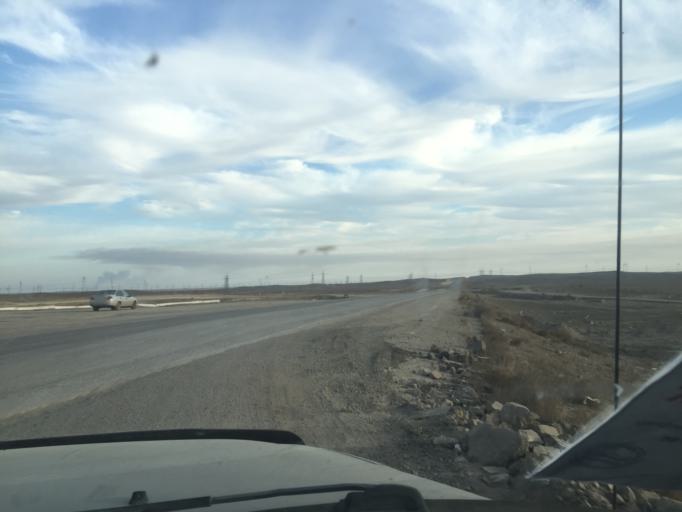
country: KZ
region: Almaty Oblysy
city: Ulken
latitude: 45.1542
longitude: 73.9496
